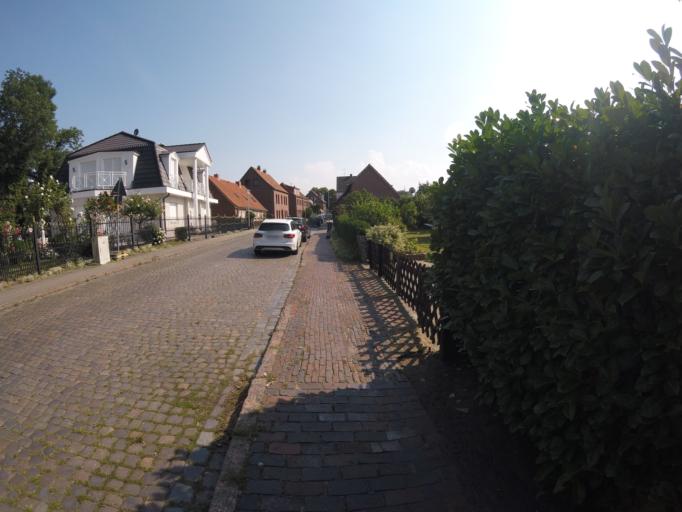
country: DE
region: Lower Saxony
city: Stade
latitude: 53.6075
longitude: 9.4750
